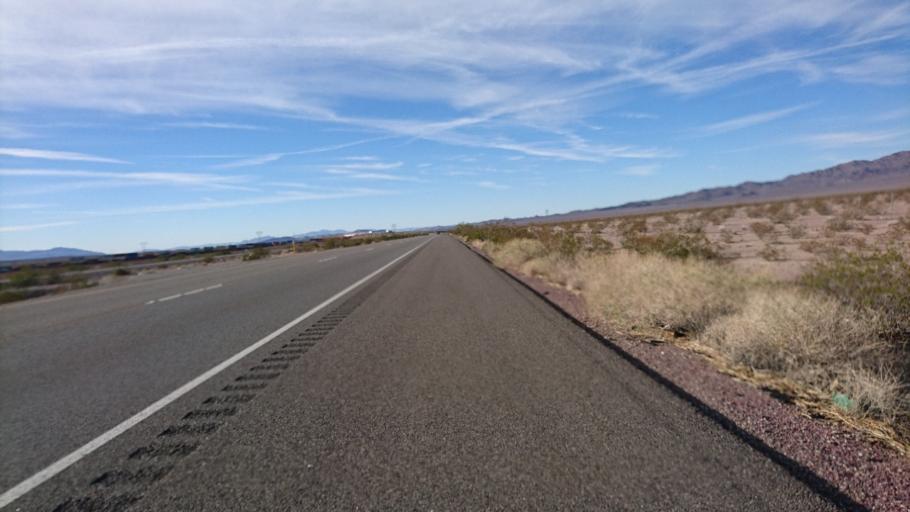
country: US
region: California
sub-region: San Bernardino County
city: Fort Irwin
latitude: 34.7669
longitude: -116.3575
